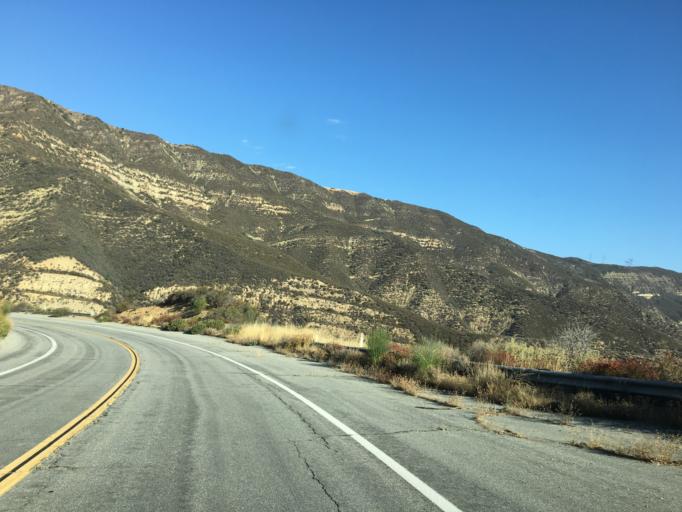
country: US
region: California
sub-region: Los Angeles County
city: Castaic
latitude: 34.5924
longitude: -118.6710
